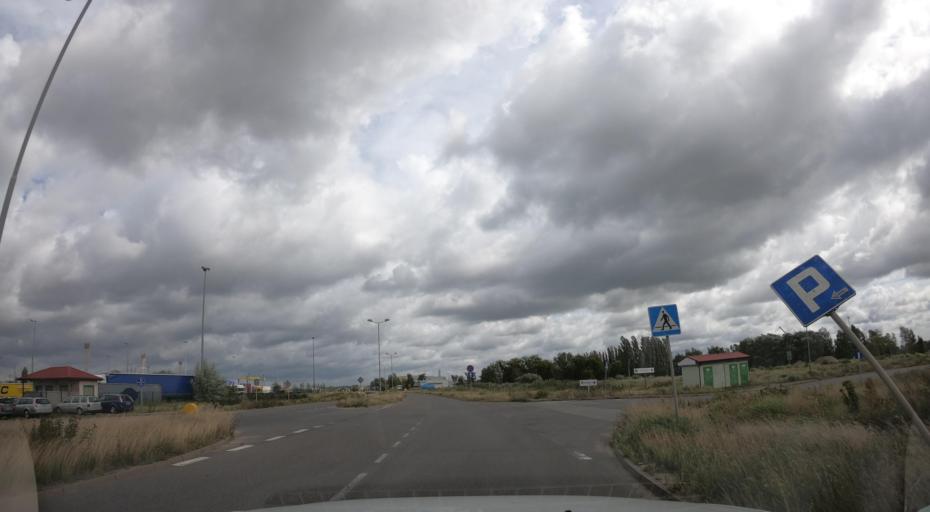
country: PL
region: West Pomeranian Voivodeship
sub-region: Szczecin
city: Szczecin
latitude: 53.4209
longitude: 14.5822
